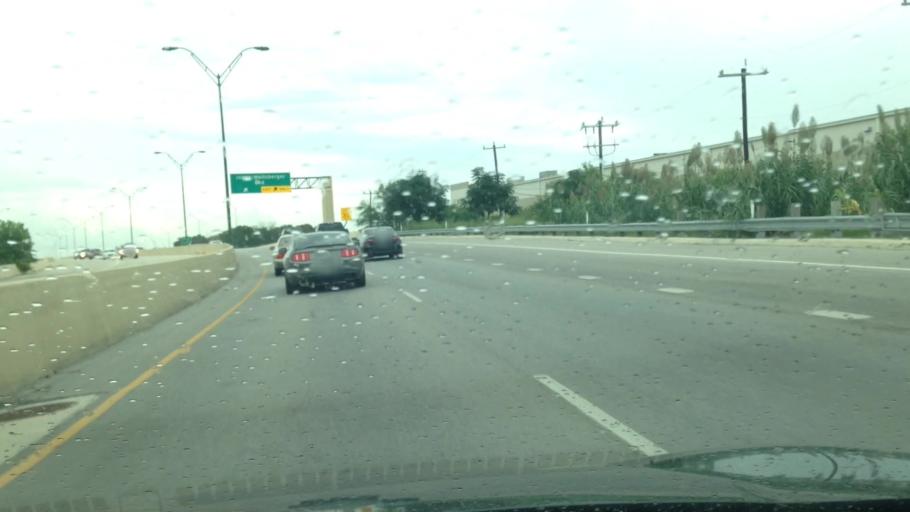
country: US
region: Texas
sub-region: Bexar County
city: Castle Hills
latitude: 29.5515
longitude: -98.4766
